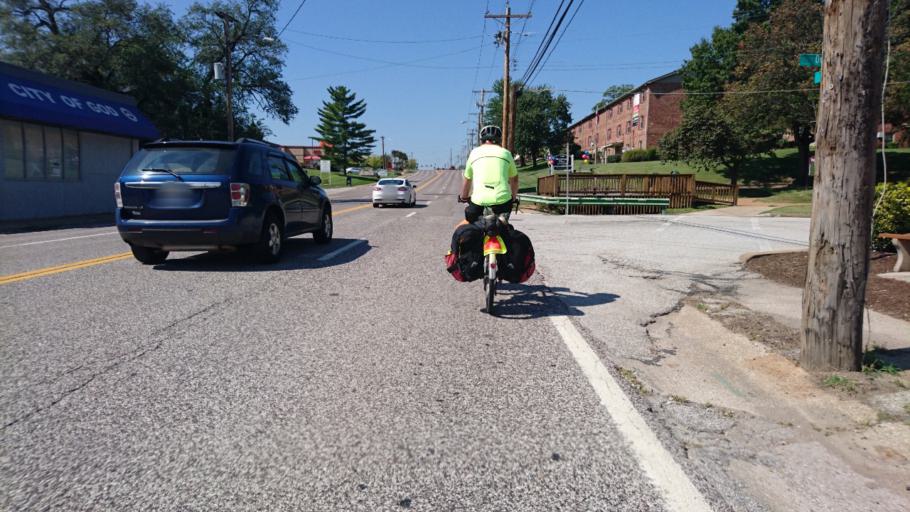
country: US
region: Missouri
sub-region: Saint Louis County
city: Brentwood
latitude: 38.6124
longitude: -90.3447
